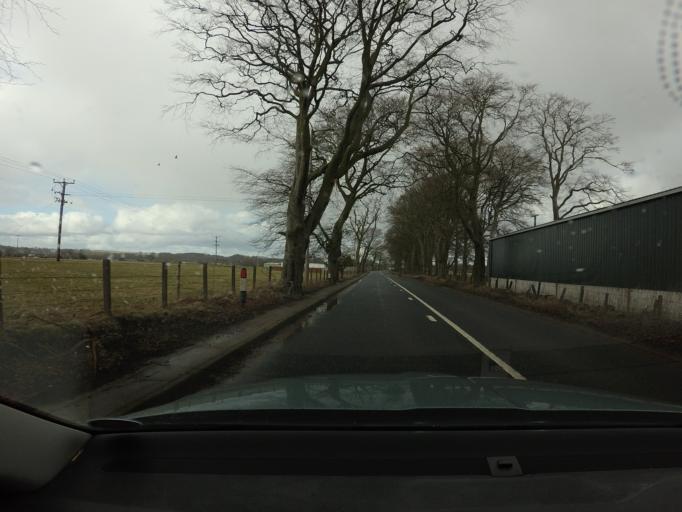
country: GB
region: Scotland
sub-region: South Lanarkshire
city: Lanark
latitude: 55.6823
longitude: -3.7157
